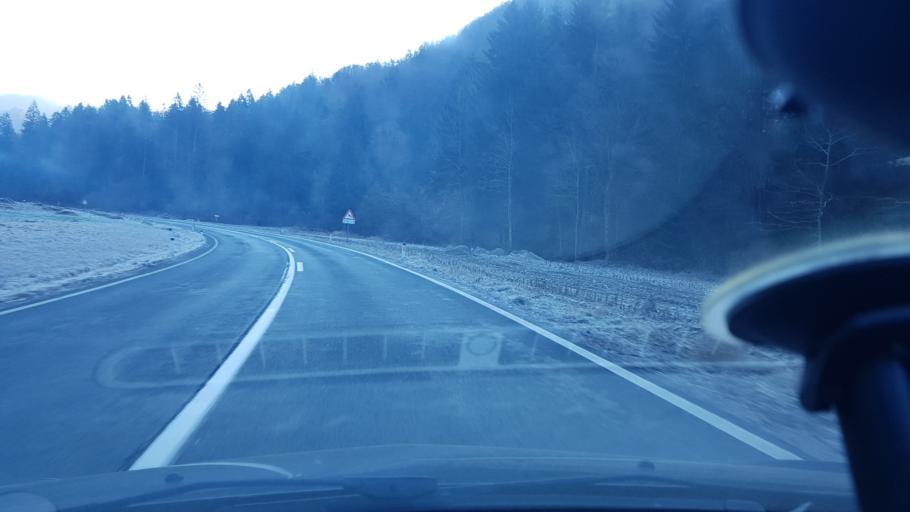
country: SI
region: Moravce
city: Moravce
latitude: 46.1737
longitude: 14.8302
